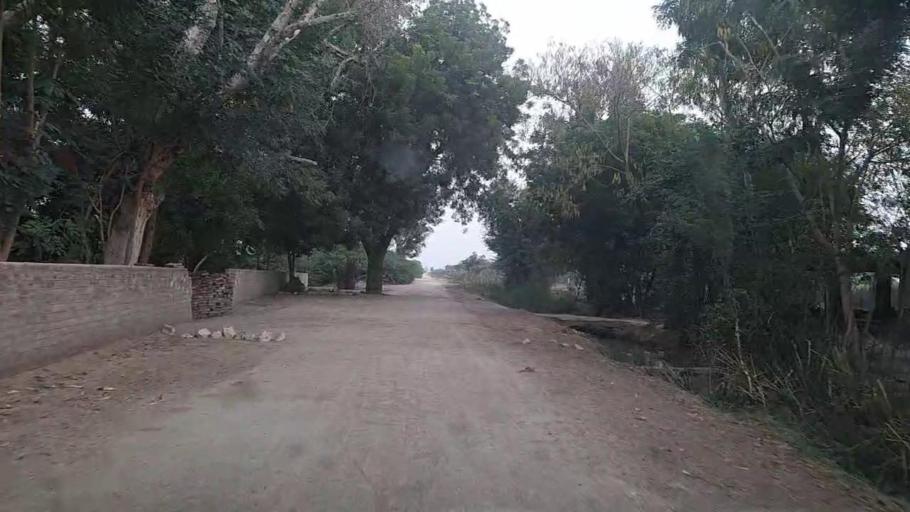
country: PK
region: Sindh
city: Gambat
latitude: 27.3738
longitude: 68.5687
